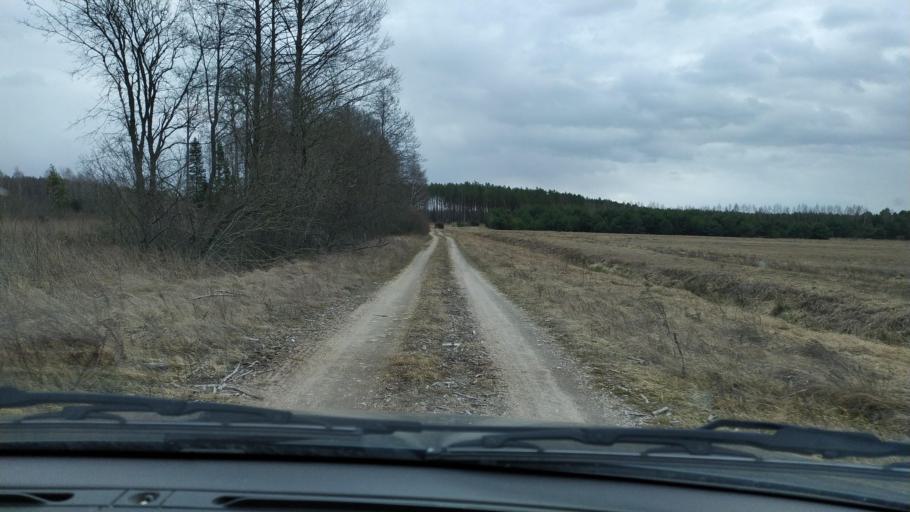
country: BY
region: Brest
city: Zhabinka
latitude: 52.4060
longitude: 24.0690
